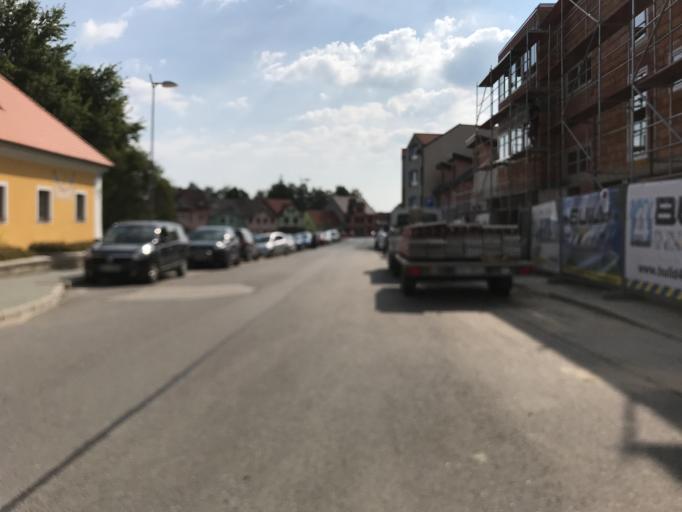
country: CZ
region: Jihocesky
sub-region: Okres Jindrichuv Hradec
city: Trebon
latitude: 49.0044
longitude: 14.7573
